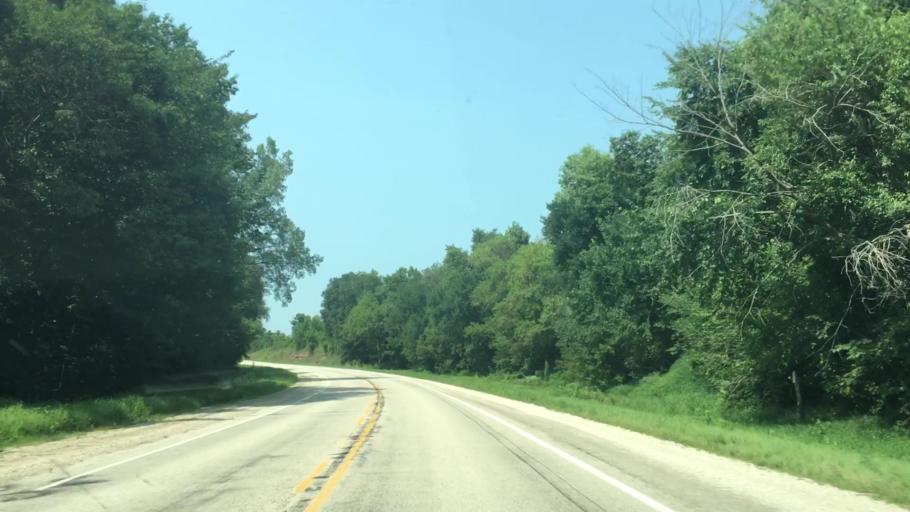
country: US
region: Iowa
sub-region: Fayette County
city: West Union
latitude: 43.0775
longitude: -91.8398
